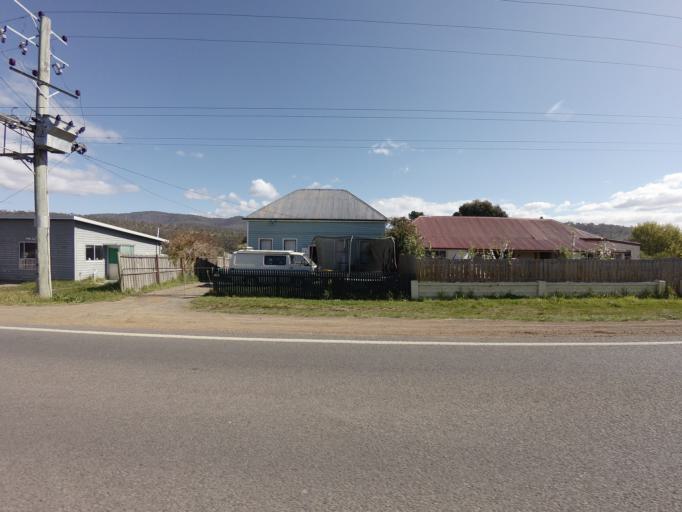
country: AU
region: Tasmania
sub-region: Derwent Valley
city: New Norfolk
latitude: -42.7709
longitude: 147.0317
